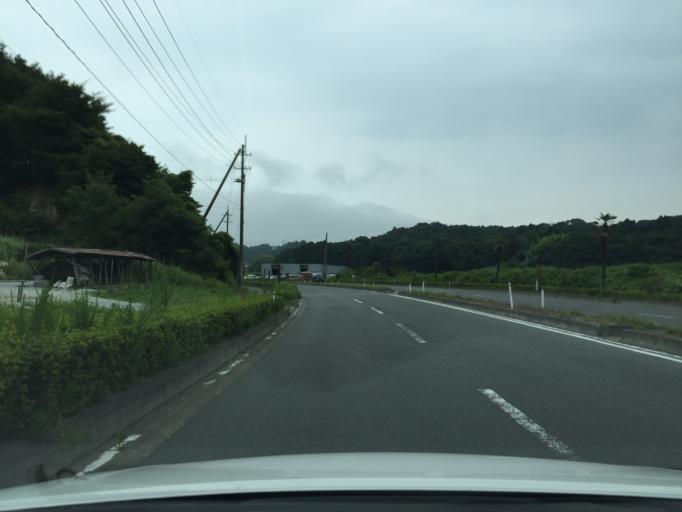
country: JP
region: Fukushima
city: Iwaki
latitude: 36.9571
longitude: 140.9189
